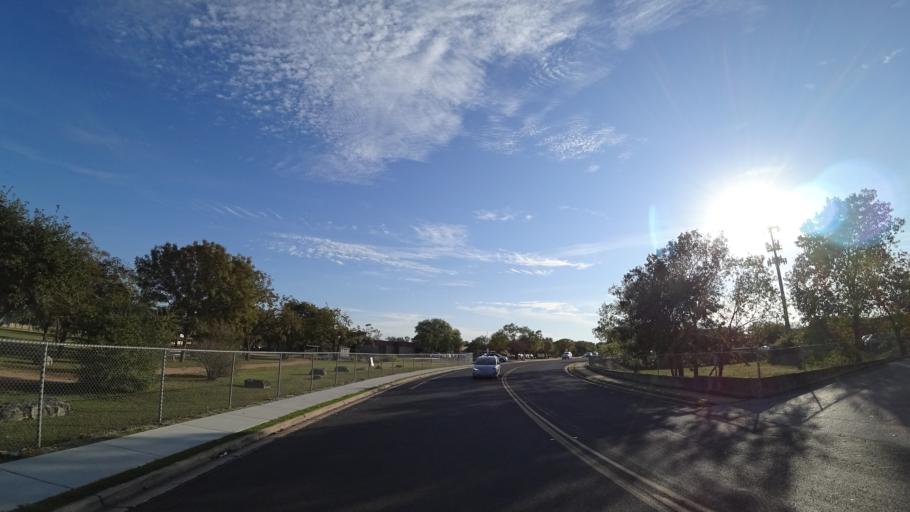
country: US
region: Texas
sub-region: Williamson County
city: Anderson Mill
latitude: 30.4465
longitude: -97.8040
